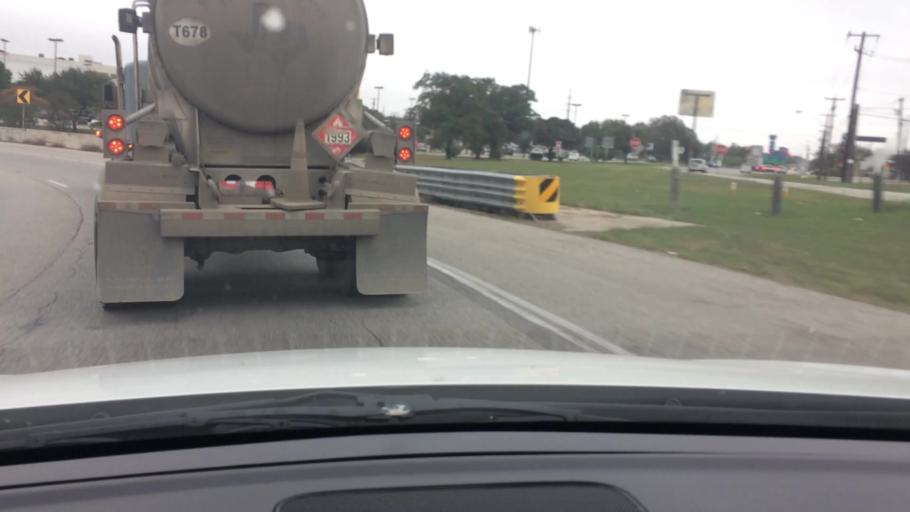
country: US
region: Texas
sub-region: Bexar County
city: Windcrest
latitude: 29.5222
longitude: -98.3927
